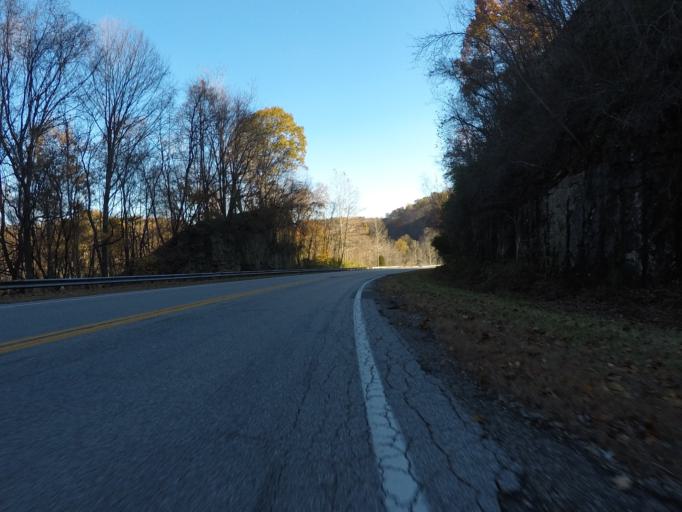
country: US
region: West Virginia
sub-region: Wayne County
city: Ceredo
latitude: 38.3819
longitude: -82.5643
